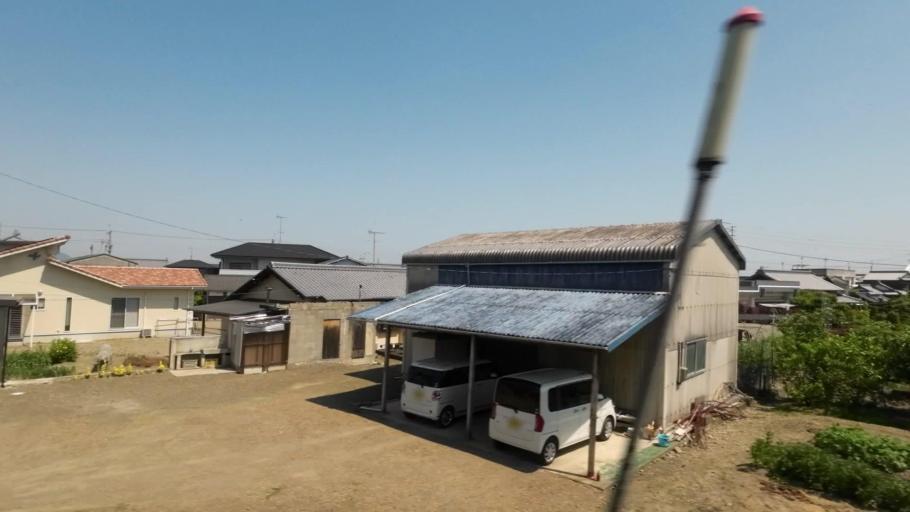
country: JP
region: Ehime
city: Saijo
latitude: 33.8983
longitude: 133.1057
